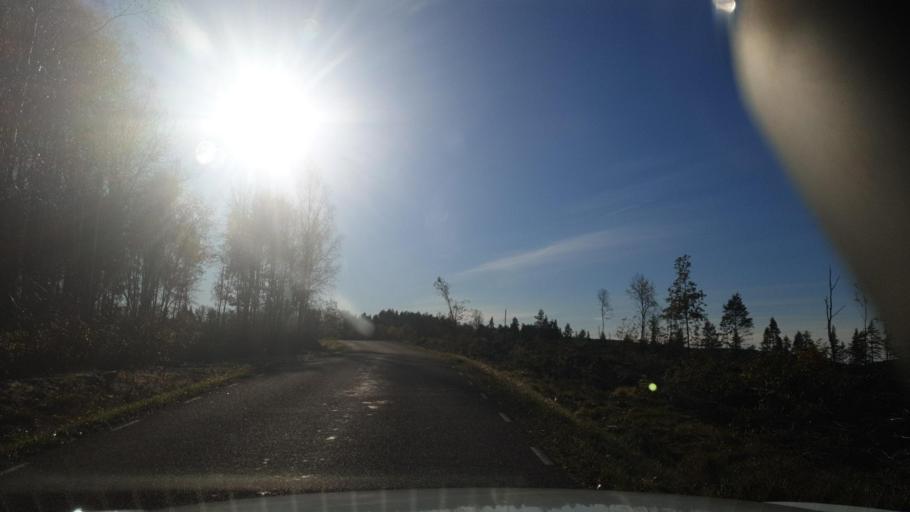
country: SE
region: Vaermland
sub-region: Grums Kommun
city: Grums
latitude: 59.4296
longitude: 13.0848
